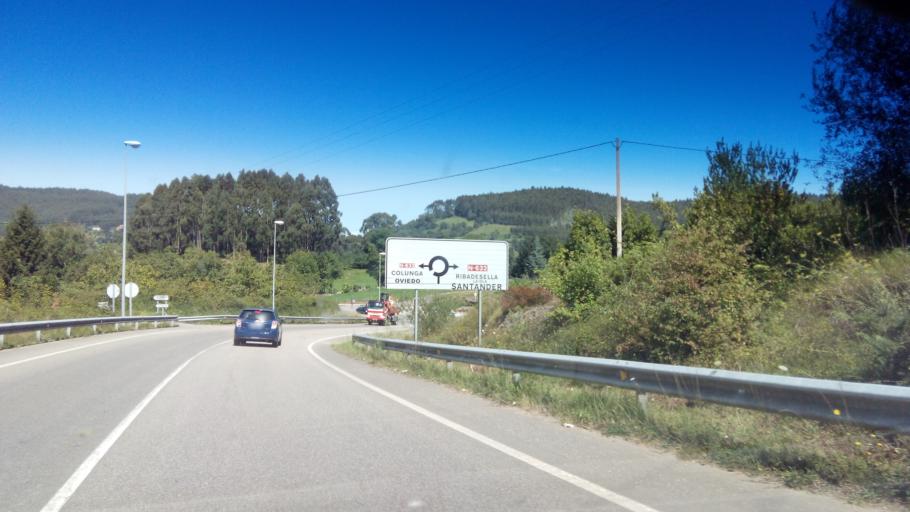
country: ES
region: Asturias
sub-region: Province of Asturias
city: Colunga
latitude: 43.4824
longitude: -5.2554
